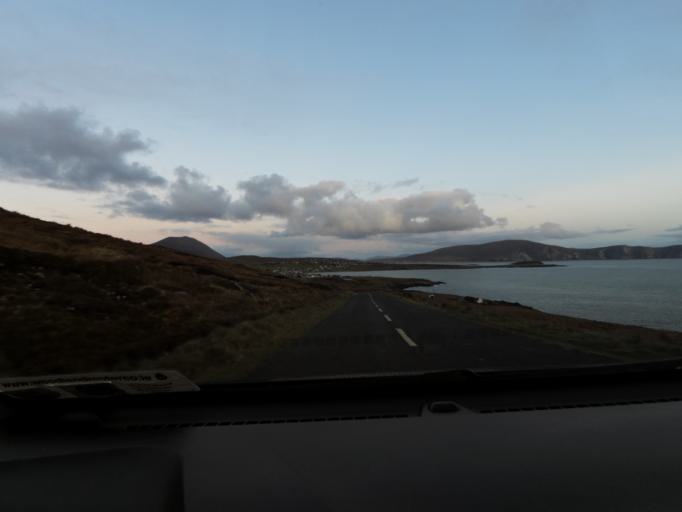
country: IE
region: Connaught
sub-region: Maigh Eo
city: Belmullet
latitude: 53.9693
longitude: -10.1553
